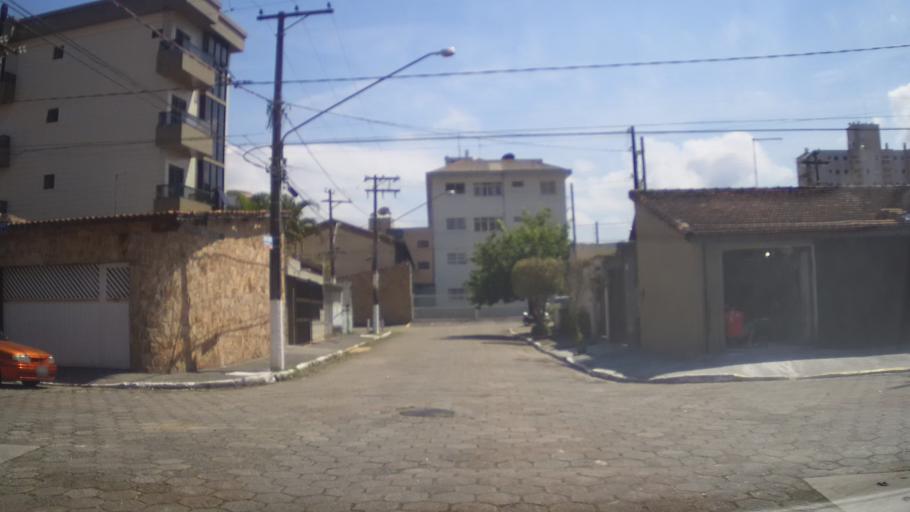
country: BR
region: Sao Paulo
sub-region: Praia Grande
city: Praia Grande
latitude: -24.0163
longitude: -46.4458
